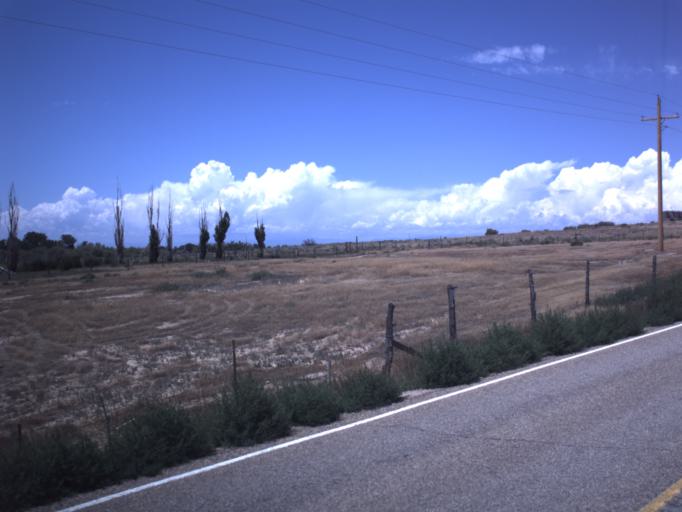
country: US
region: Utah
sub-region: Uintah County
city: Naples
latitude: 40.1507
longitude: -109.6641
